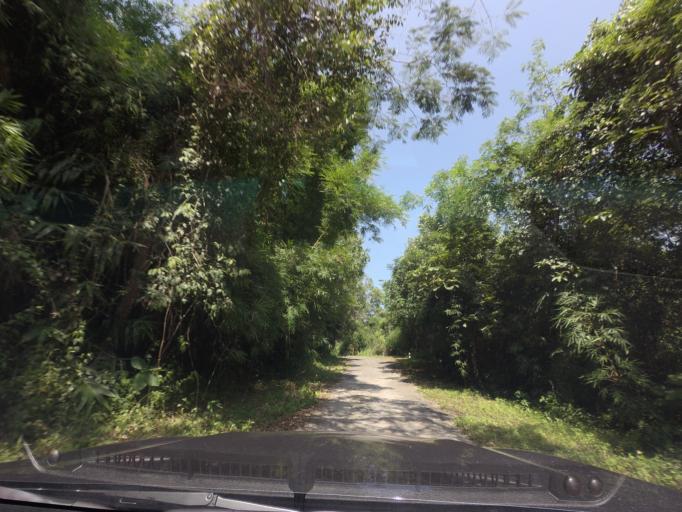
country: TH
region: Loei
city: Na Haeo
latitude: 17.5693
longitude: 100.9774
